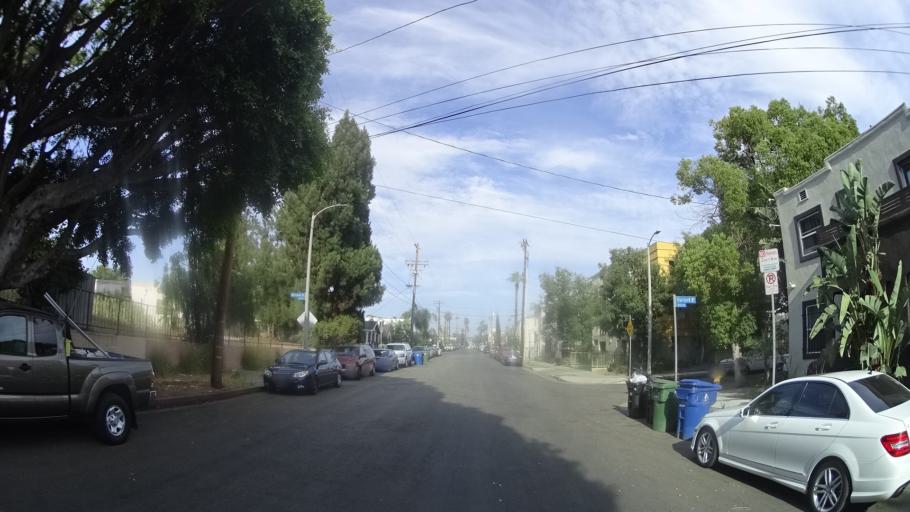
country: US
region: California
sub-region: Los Angeles County
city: Hollywood
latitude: 34.0885
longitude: -118.3043
